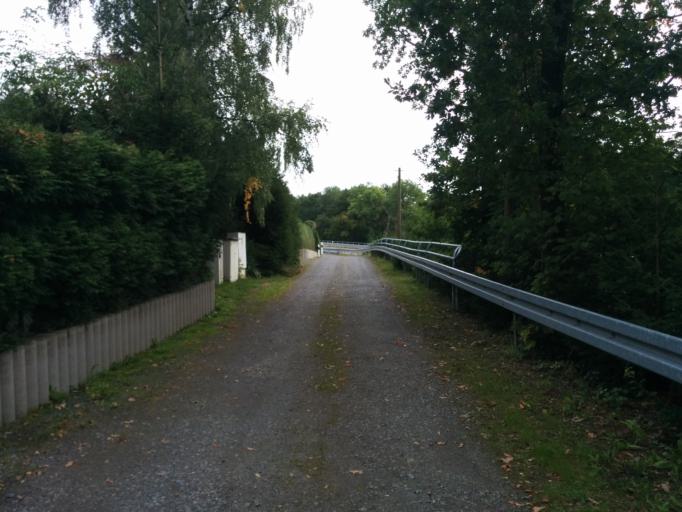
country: DE
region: Saxony
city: Floha
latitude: 50.8504
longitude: 13.0812
